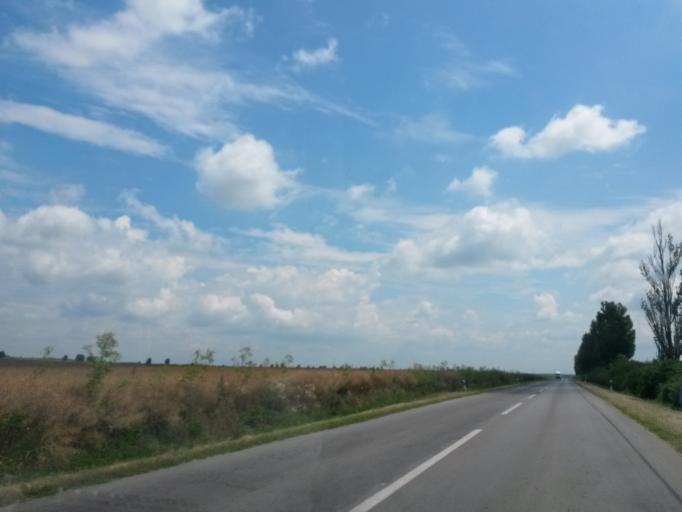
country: HR
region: Osjecko-Baranjska
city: Dalj
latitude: 45.5113
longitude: 18.9316
